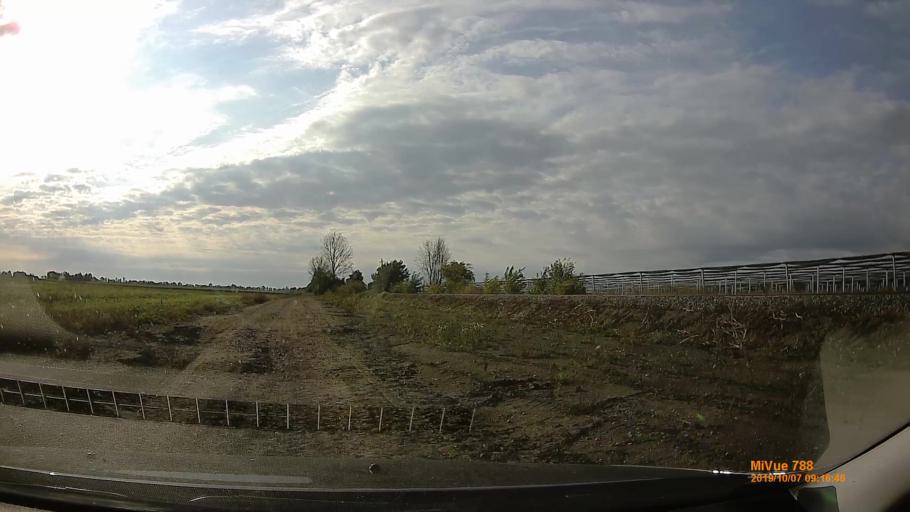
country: HU
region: Bekes
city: Nagyszenas
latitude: 46.8107
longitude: 20.6743
